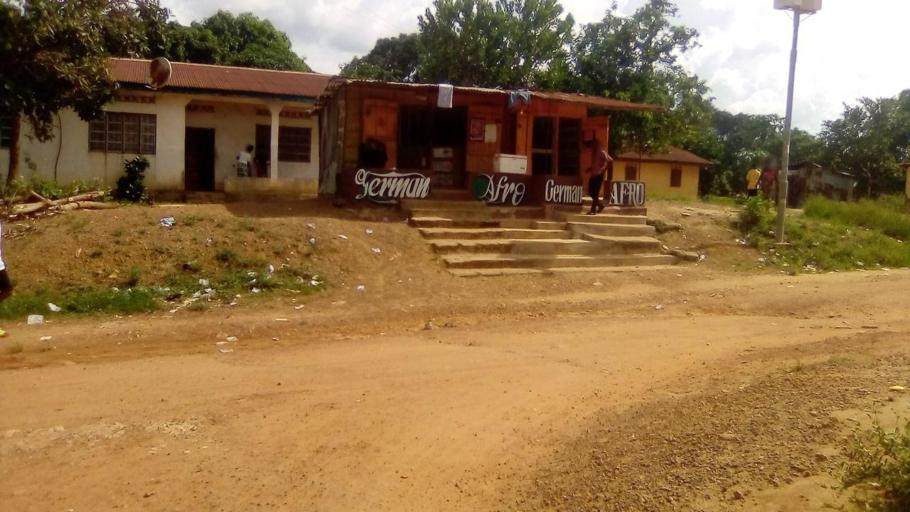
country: SL
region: Southern Province
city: Bo
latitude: 7.9500
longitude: -11.7231
